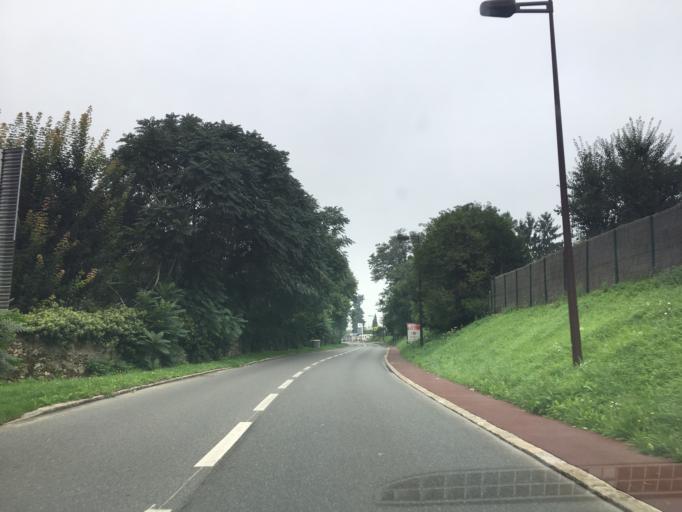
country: FR
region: Ile-de-France
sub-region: Departement de l'Essonne
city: Etiolles
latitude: 48.6278
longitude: 2.4724
